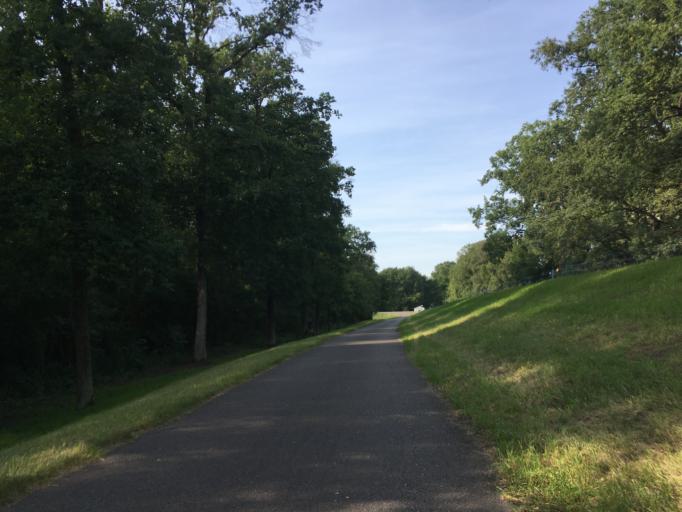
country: DE
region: Brandenburg
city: Brieskow-Finkenheerd
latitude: 52.2737
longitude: 14.5914
